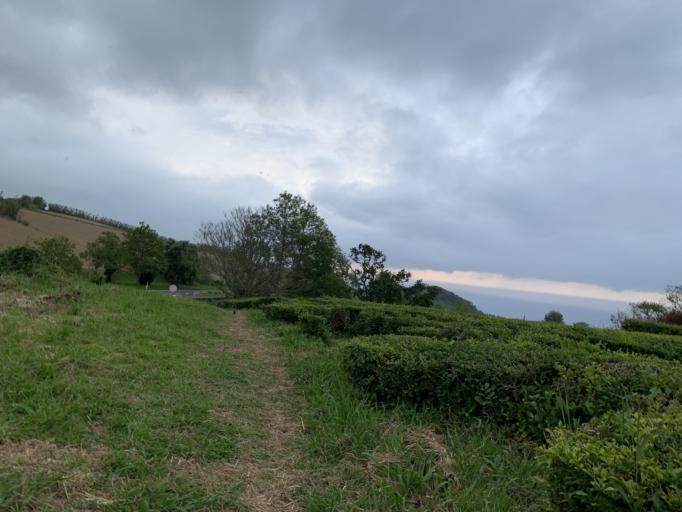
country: PT
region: Azores
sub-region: Povoacao
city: Furnas
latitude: 37.8172
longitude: -25.4022
